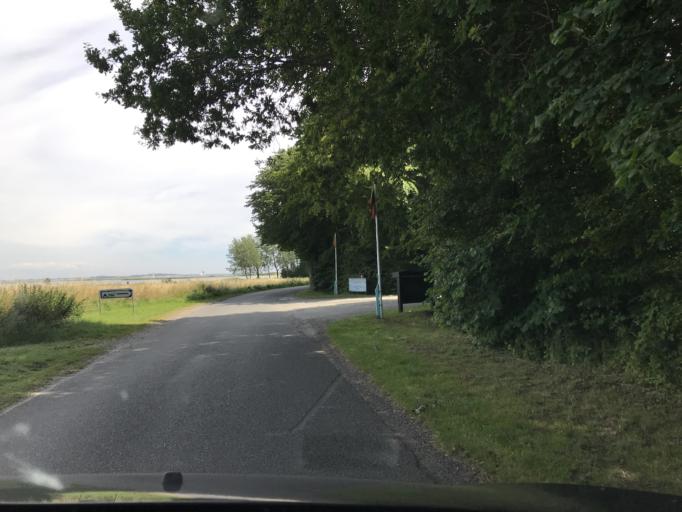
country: DK
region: South Denmark
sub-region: AEro Kommune
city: Marstal
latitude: 54.8474
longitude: 10.5182
